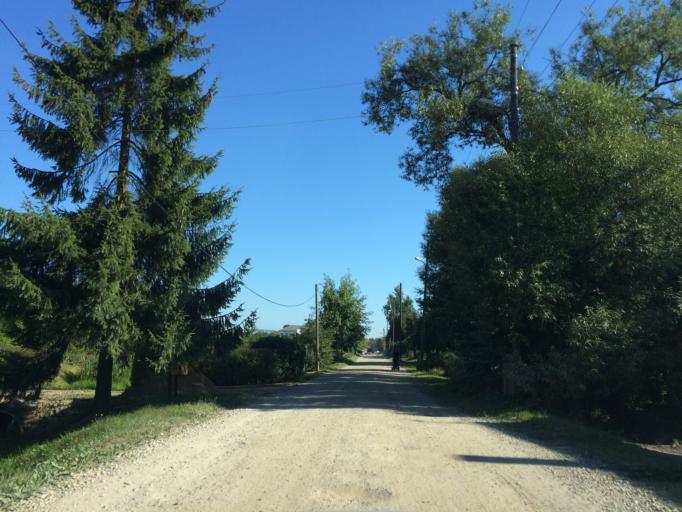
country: LV
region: Rezekne
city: Rezekne
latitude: 56.4964
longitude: 27.3279
